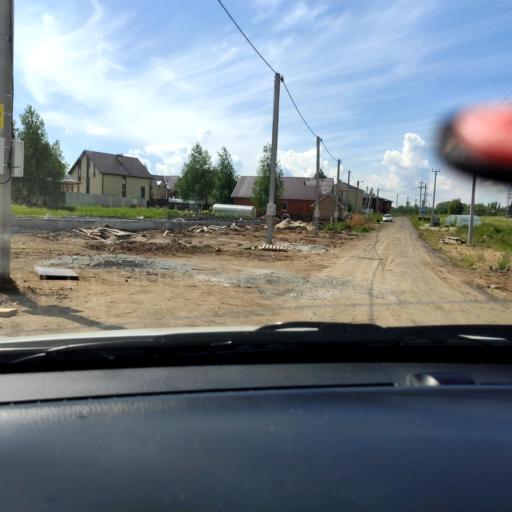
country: RU
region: Tatarstan
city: Stolbishchi
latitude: 55.7253
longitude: 49.3117
